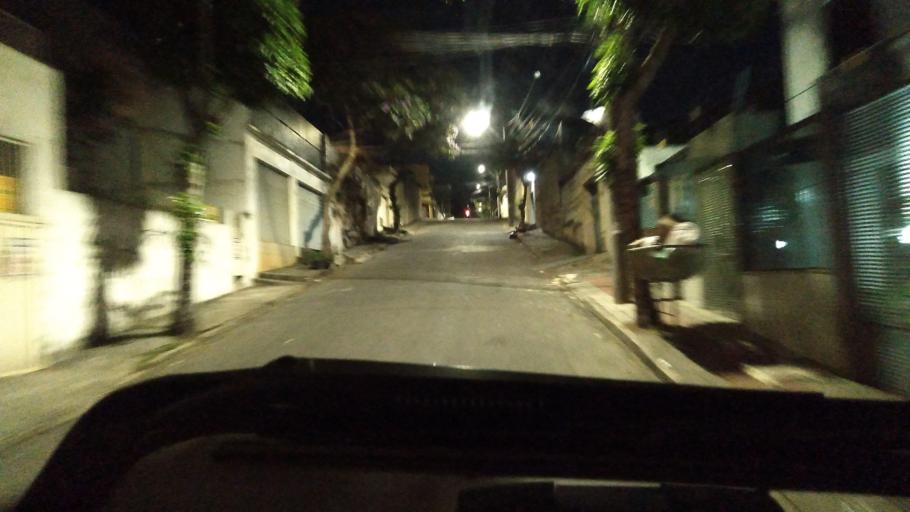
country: BR
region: Minas Gerais
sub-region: Belo Horizonte
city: Belo Horizonte
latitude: -19.9186
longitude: -43.9808
